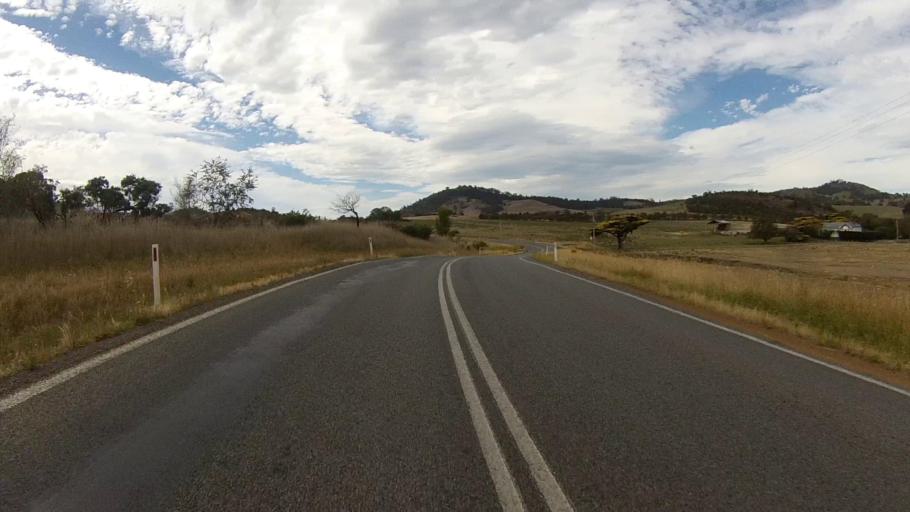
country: AU
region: Tasmania
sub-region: Sorell
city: Sorell
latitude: -42.6931
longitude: 147.4761
